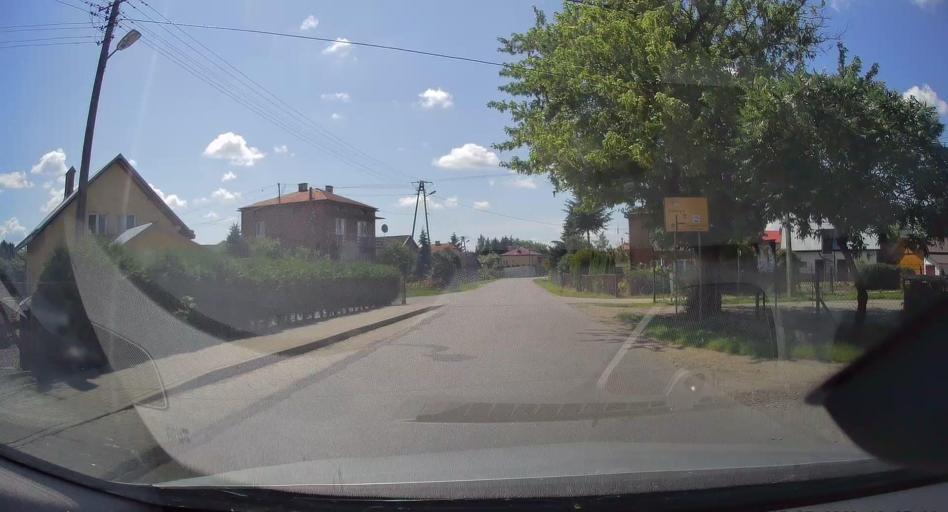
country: PL
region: Subcarpathian Voivodeship
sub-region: Powiat przemyski
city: Medyka
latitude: 49.8224
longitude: 22.8661
